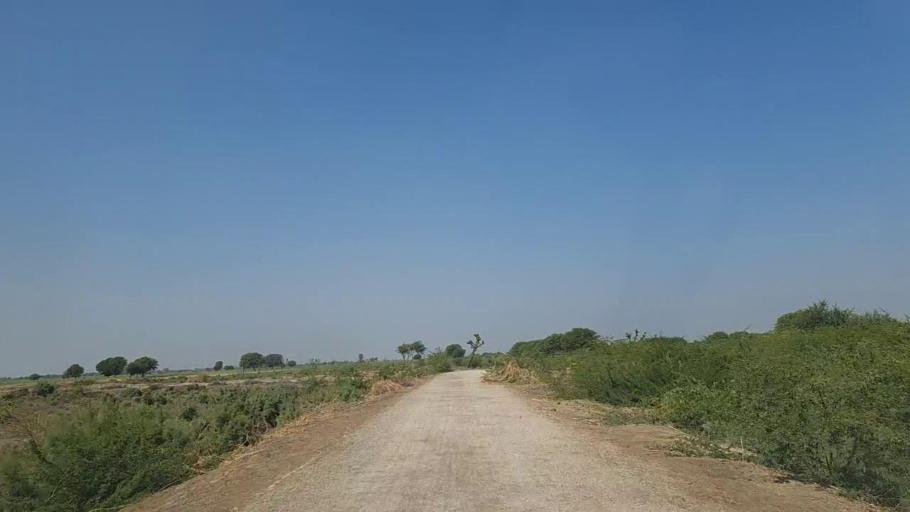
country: PK
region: Sindh
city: Digri
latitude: 25.1963
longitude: 69.1391
